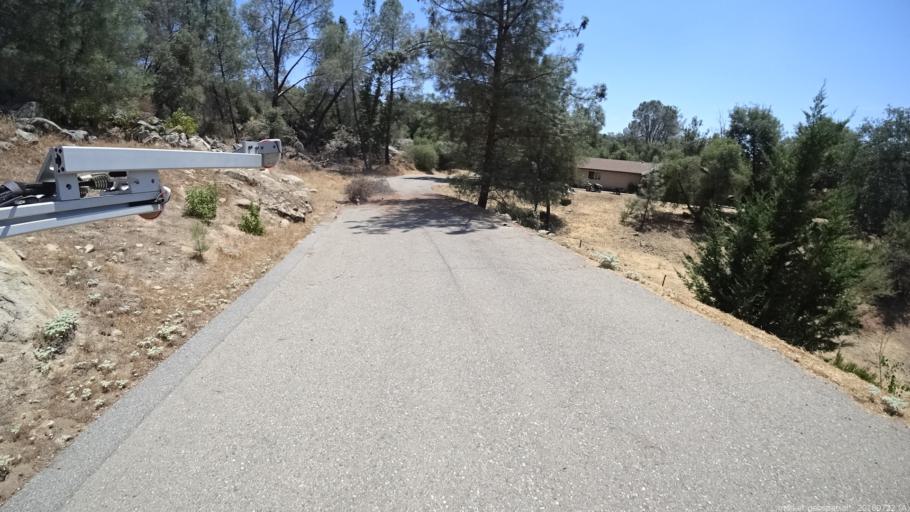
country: US
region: California
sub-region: Madera County
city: Yosemite Lakes
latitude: 37.2064
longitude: -119.7247
